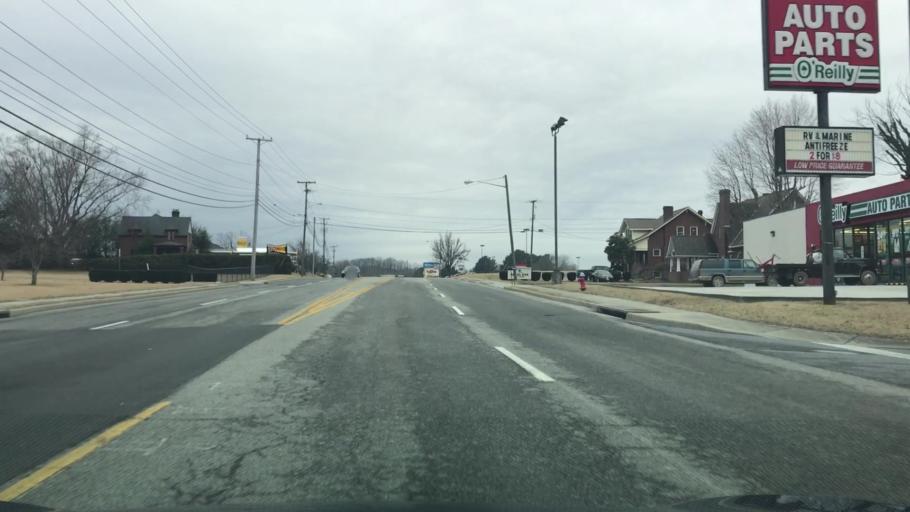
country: US
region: Virginia
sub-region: Smyth County
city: Marion
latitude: 36.8452
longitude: -81.4979
